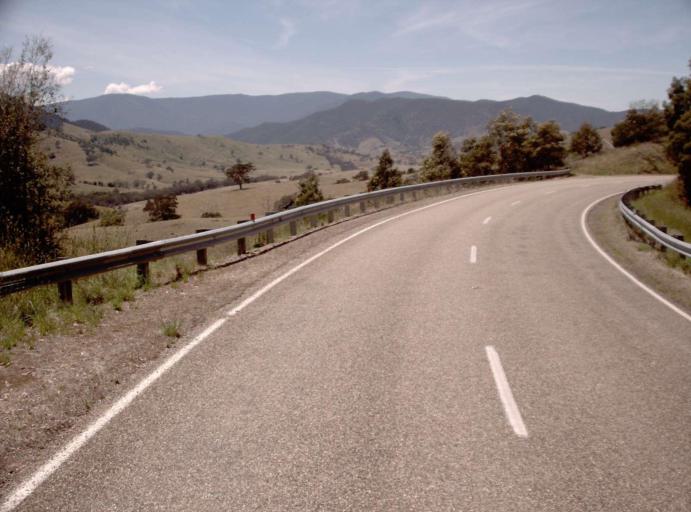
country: AU
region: Victoria
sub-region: Alpine
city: Mount Beauty
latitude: -37.1635
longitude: 147.6654
